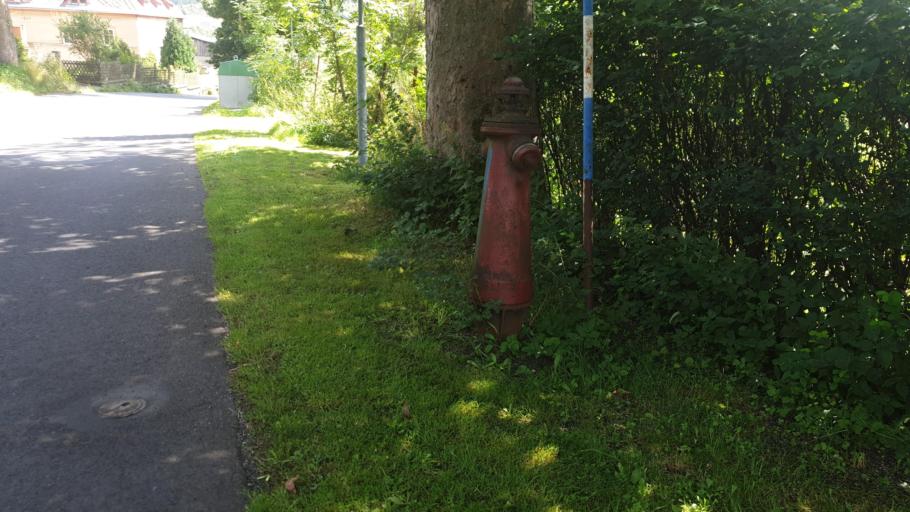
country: CZ
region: Ustecky
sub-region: Okres Chomutov
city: Kovarska
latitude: 50.4355
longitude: 13.0449
